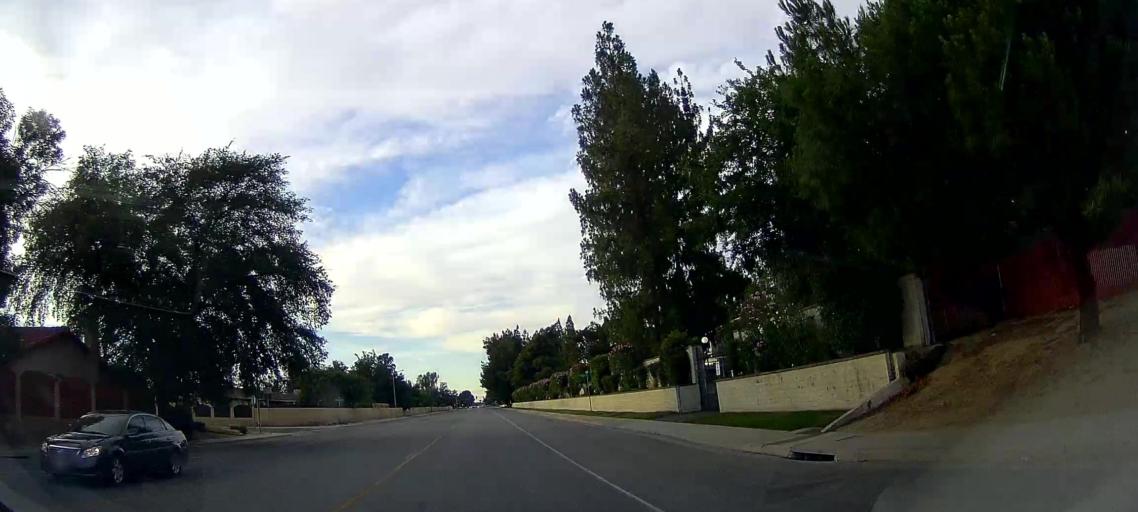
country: US
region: California
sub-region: Kern County
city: Bakersfield
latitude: 35.3214
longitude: -119.0478
